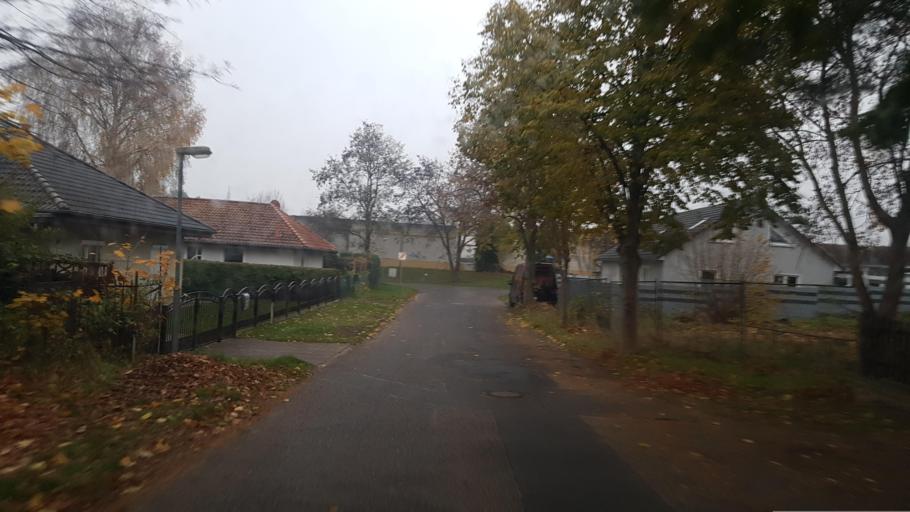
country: DE
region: Brandenburg
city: Michendorf
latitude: 52.3045
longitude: 13.0201
